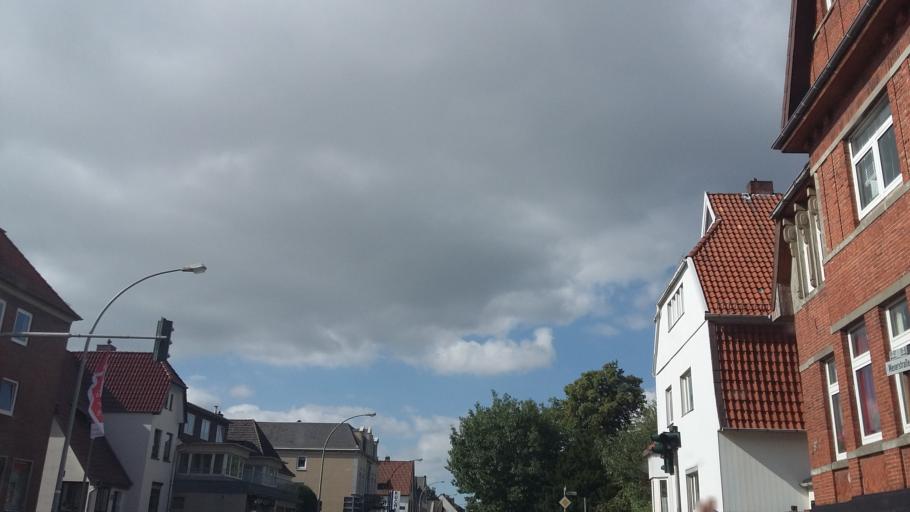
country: DE
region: Bremen
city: Bremerhaven
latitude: 53.5067
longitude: 8.5981
